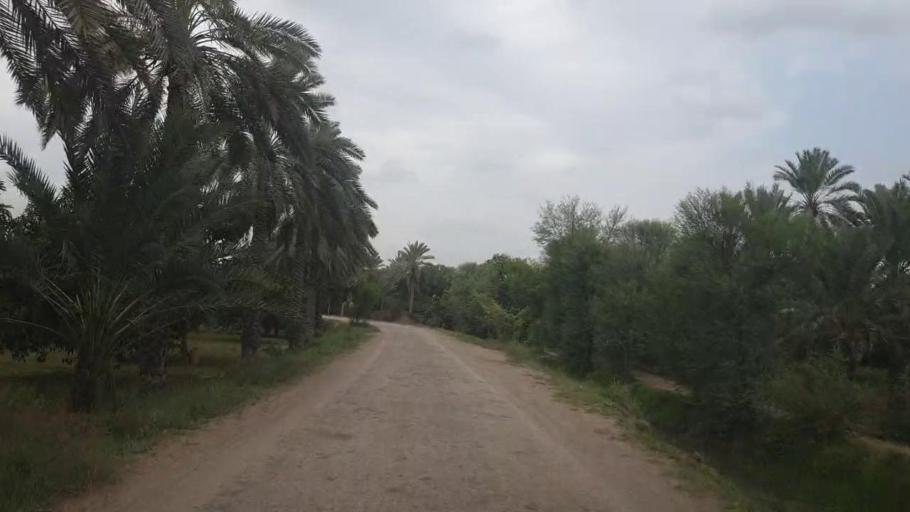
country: PK
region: Sindh
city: Khairpur
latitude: 27.5734
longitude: 68.7051
